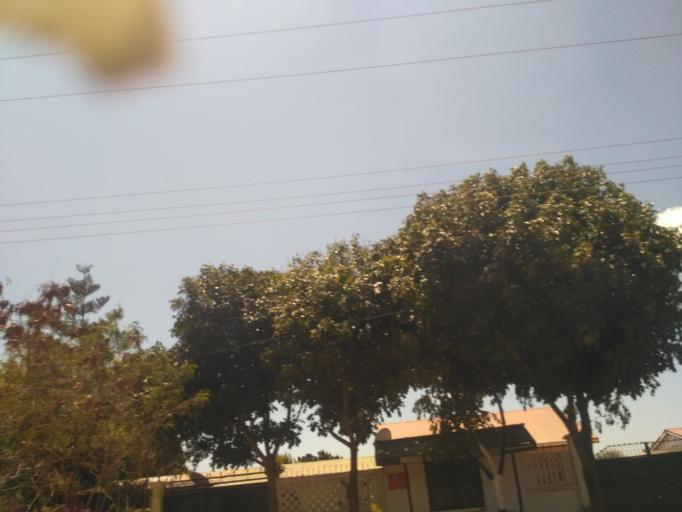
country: TZ
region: Dodoma
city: Dodoma
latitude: -6.1907
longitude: 35.7387
